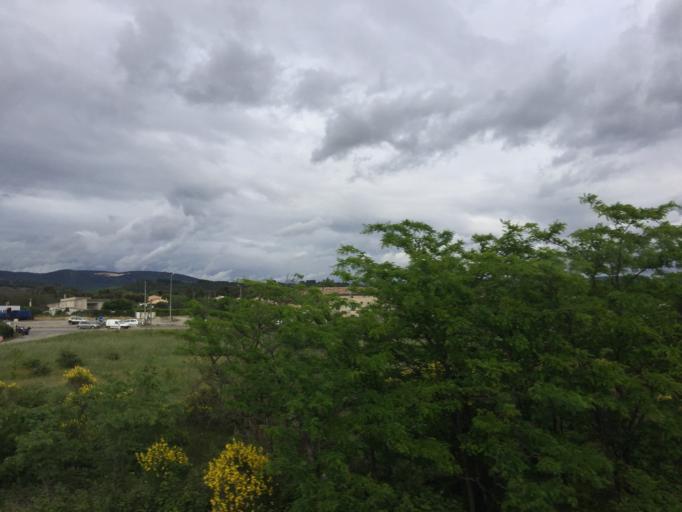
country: FR
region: Rhone-Alpes
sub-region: Departement de la Drome
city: Donzere
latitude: 44.4242
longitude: 4.7104
